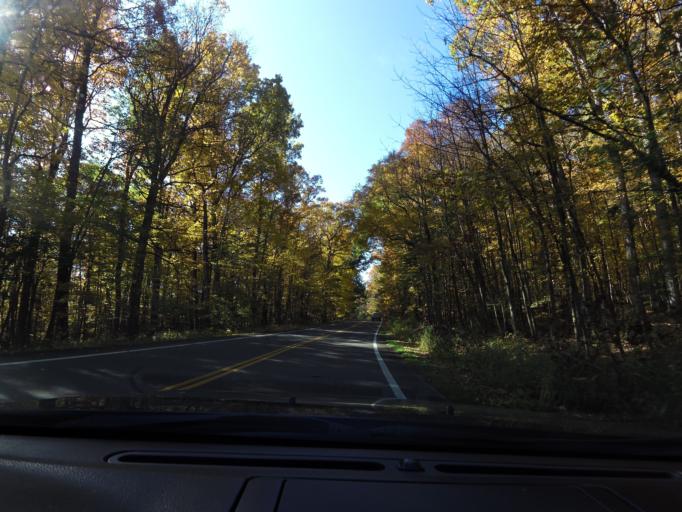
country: US
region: New York
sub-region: Wyoming County
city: Castile
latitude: 42.6460
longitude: -77.9842
